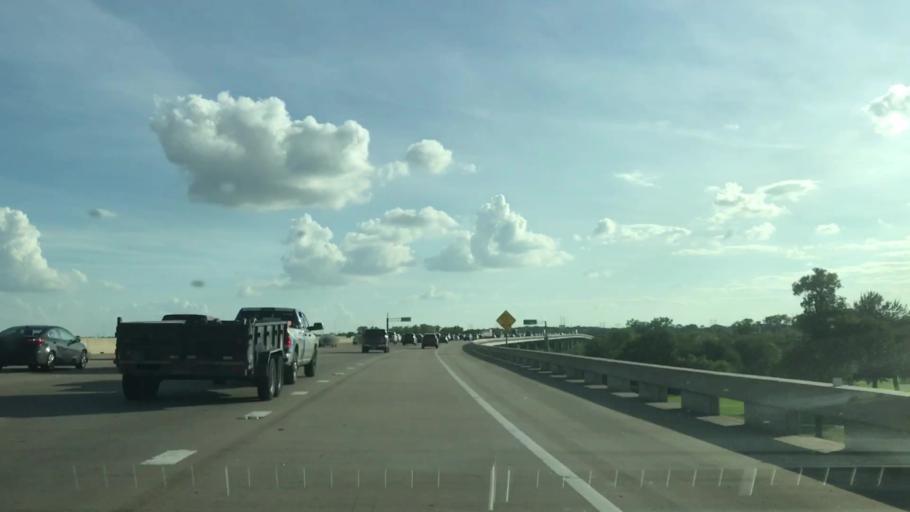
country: US
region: Texas
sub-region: Dallas County
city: Grand Prairie
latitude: 32.7855
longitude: -97.0205
